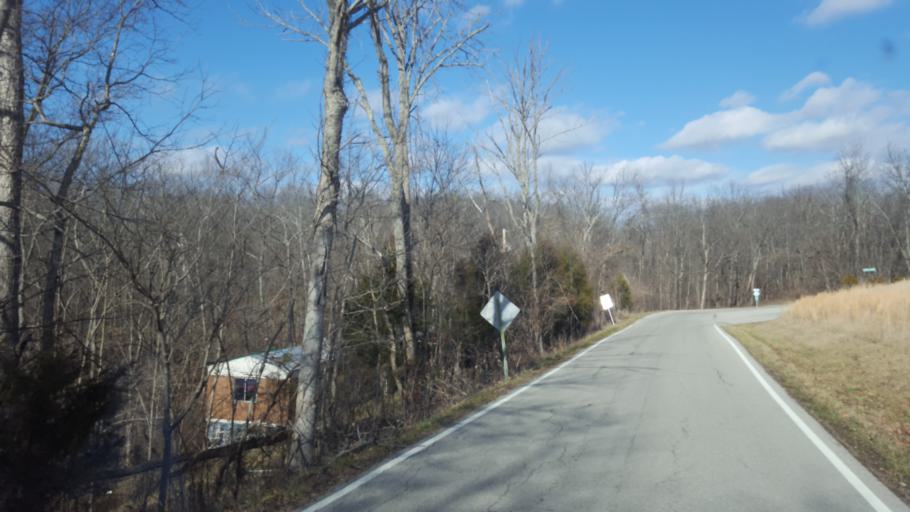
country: US
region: Kentucky
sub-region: Franklin County
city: Frankfort
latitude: 38.2844
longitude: -84.9001
